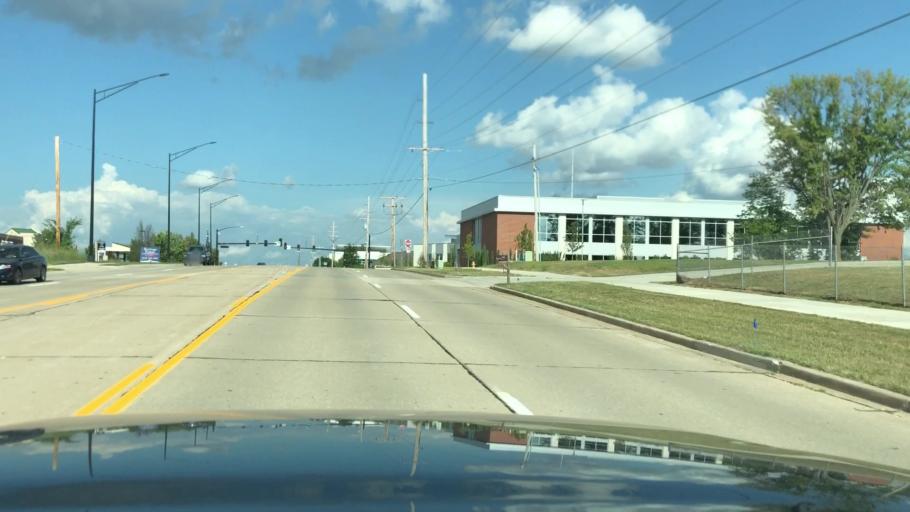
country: US
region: Missouri
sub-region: Saint Charles County
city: Wentzville
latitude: 38.8247
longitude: -90.8698
